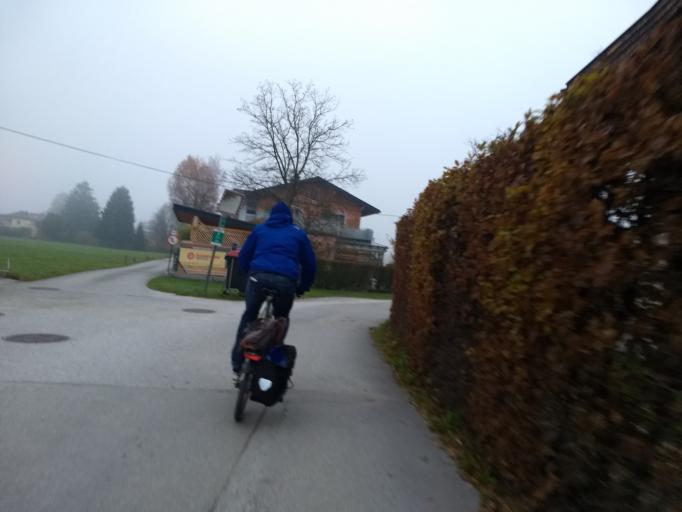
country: AT
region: Salzburg
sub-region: Salzburg Stadt
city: Salzburg
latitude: 47.7704
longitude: 13.0433
